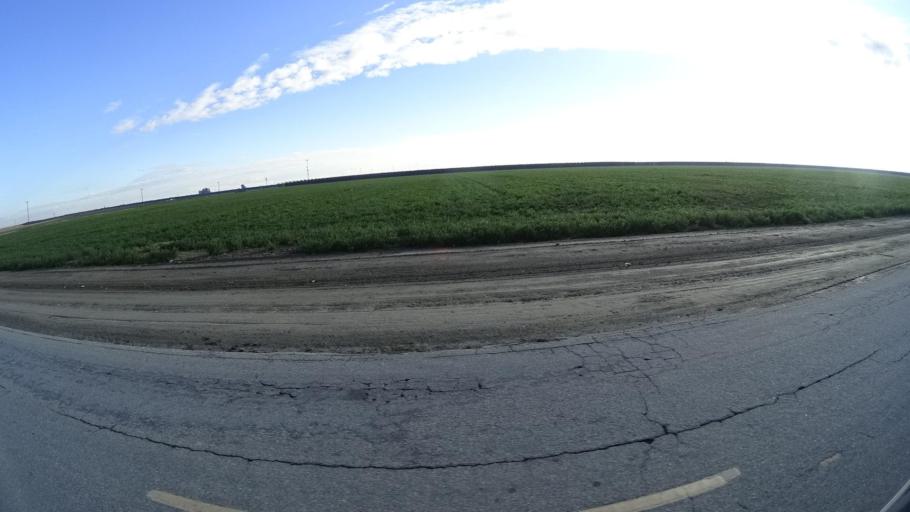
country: US
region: California
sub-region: Kern County
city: Delano
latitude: 35.7489
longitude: -119.3300
